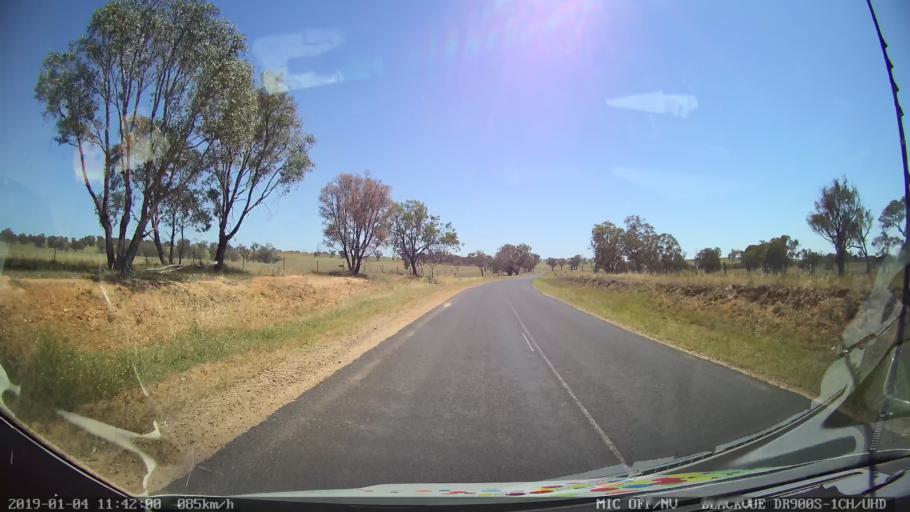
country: AU
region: New South Wales
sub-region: Cabonne
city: Molong
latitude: -32.9870
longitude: 148.7865
